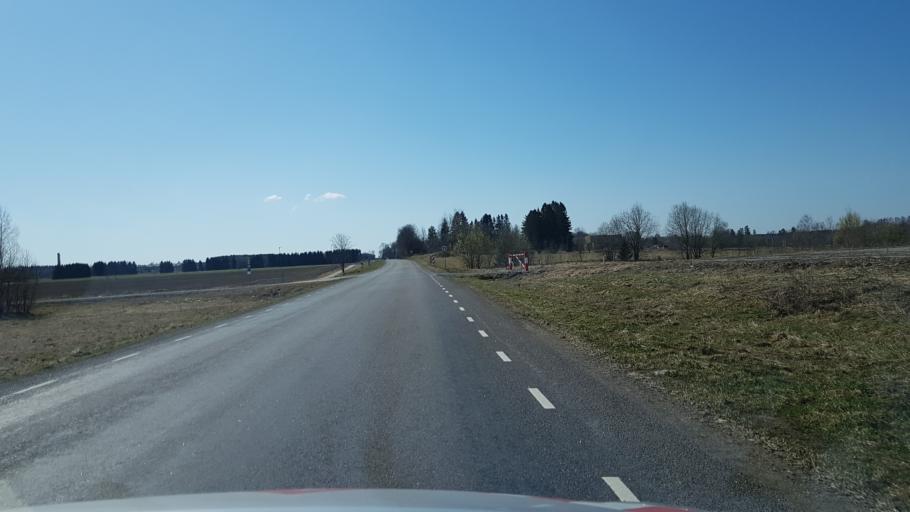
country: EE
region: Ida-Virumaa
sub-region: Kohtla-Nomme vald
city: Kohtla-Nomme
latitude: 59.2908
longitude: 27.2364
